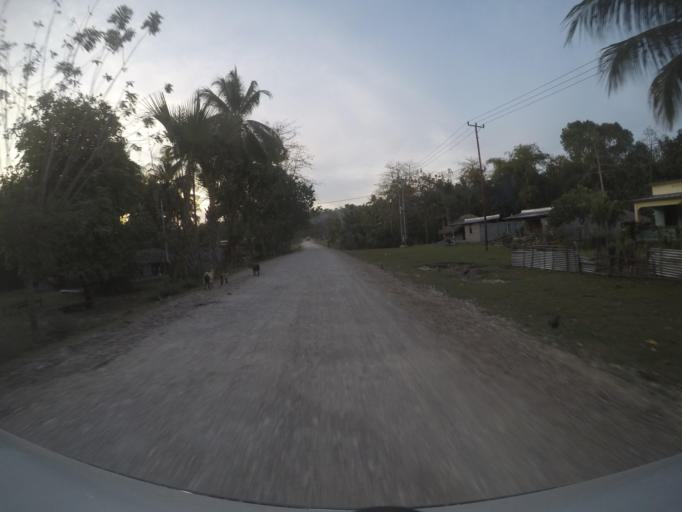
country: TL
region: Viqueque
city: Viqueque
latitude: -8.8982
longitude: 126.3921
